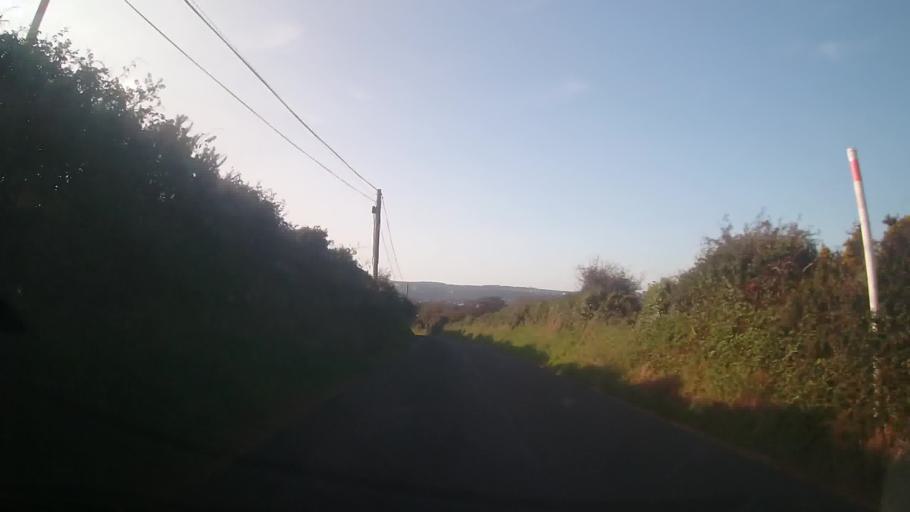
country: GB
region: Wales
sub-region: Pembrokeshire
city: Fishguard
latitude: 51.9892
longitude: -4.9636
